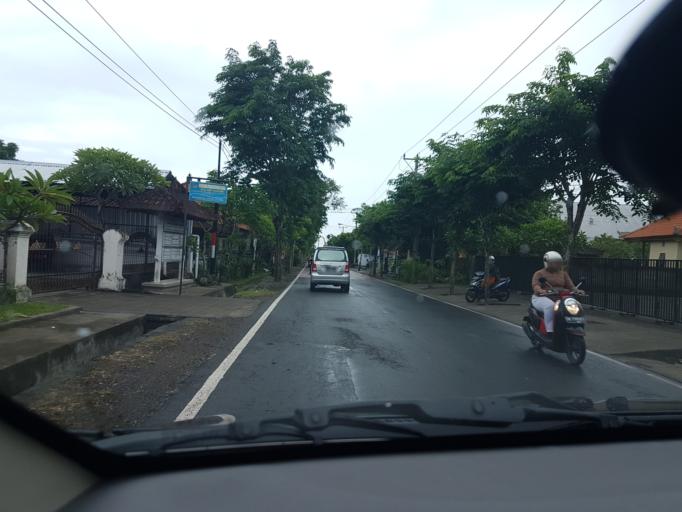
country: ID
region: Bali
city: Banjar Desa
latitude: -8.5778
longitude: 115.2387
